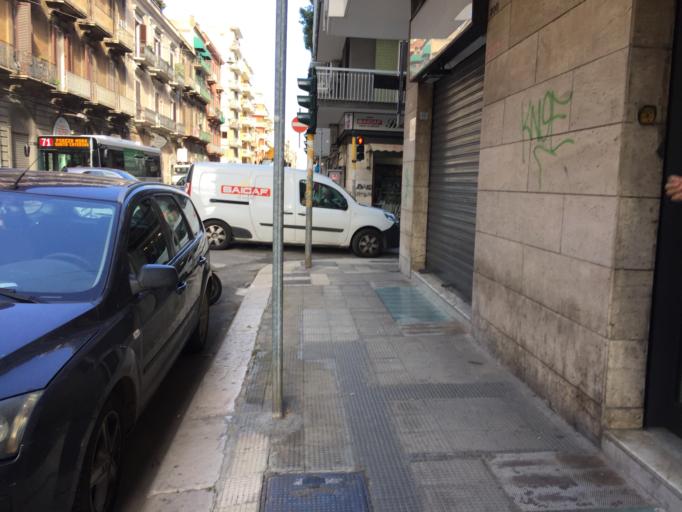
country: IT
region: Apulia
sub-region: Provincia di Bari
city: Bari
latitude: 41.1201
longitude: 16.8645
